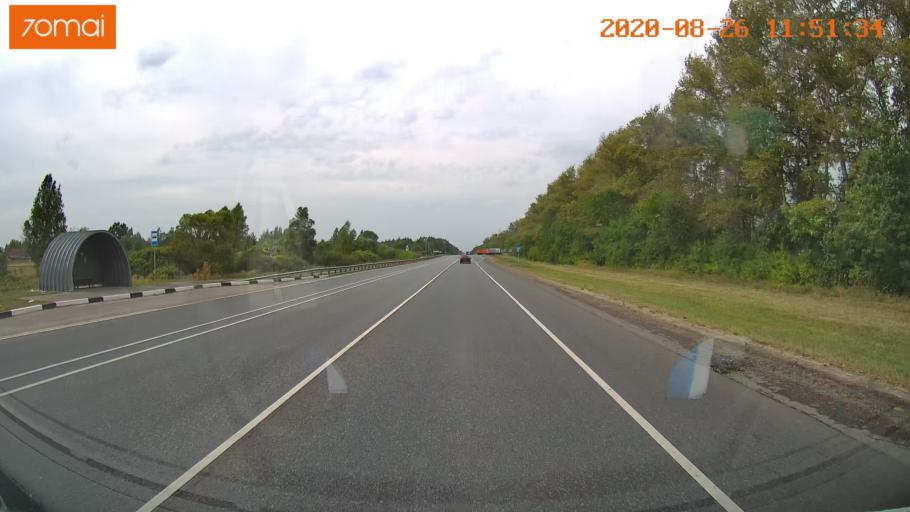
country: RU
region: Rjazan
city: Lesnoy
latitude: 54.2969
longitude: 40.4763
